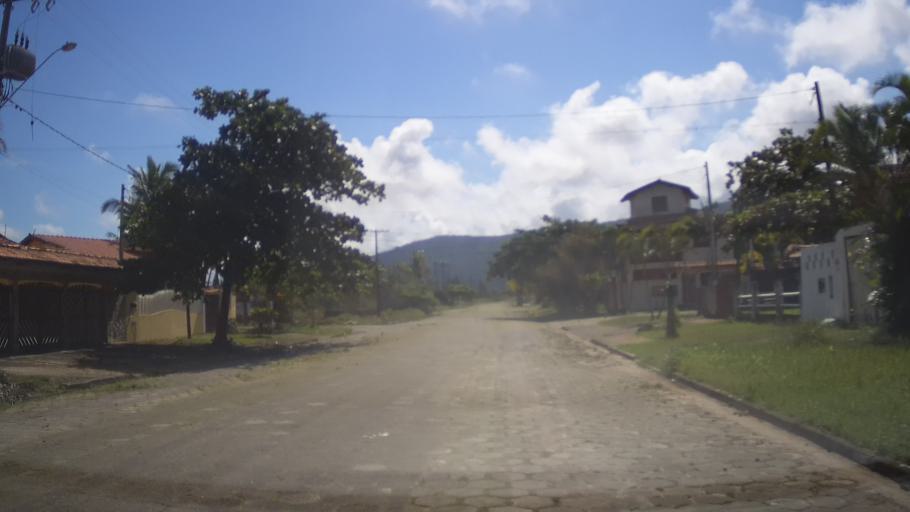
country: BR
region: Sao Paulo
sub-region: Itanhaem
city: Itanhaem
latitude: -24.1528
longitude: -46.7277
